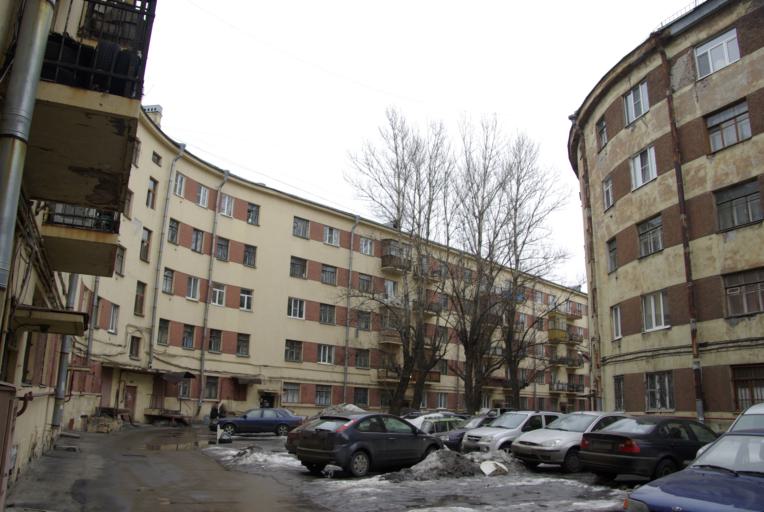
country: RU
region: St.-Petersburg
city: Admiralteisky
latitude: 59.9083
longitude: 30.2644
